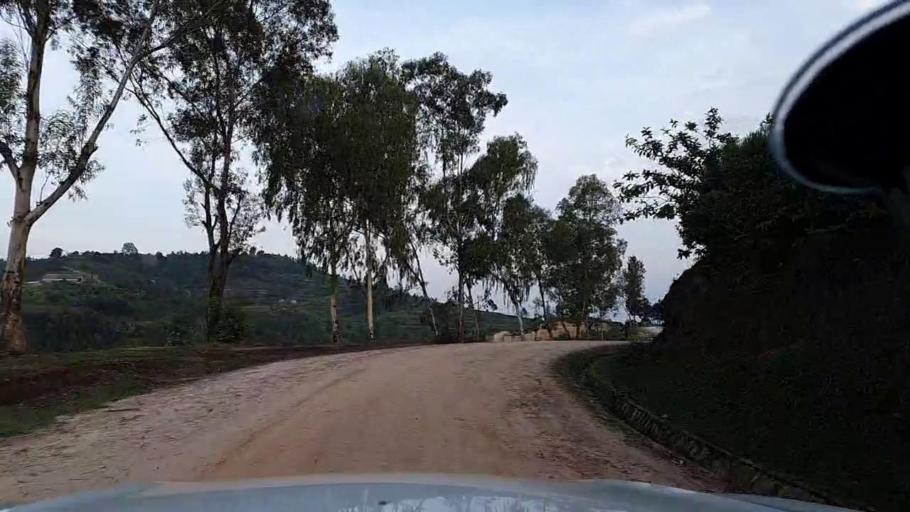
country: RW
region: Southern Province
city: Nyanza
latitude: -2.2230
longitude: 29.6497
